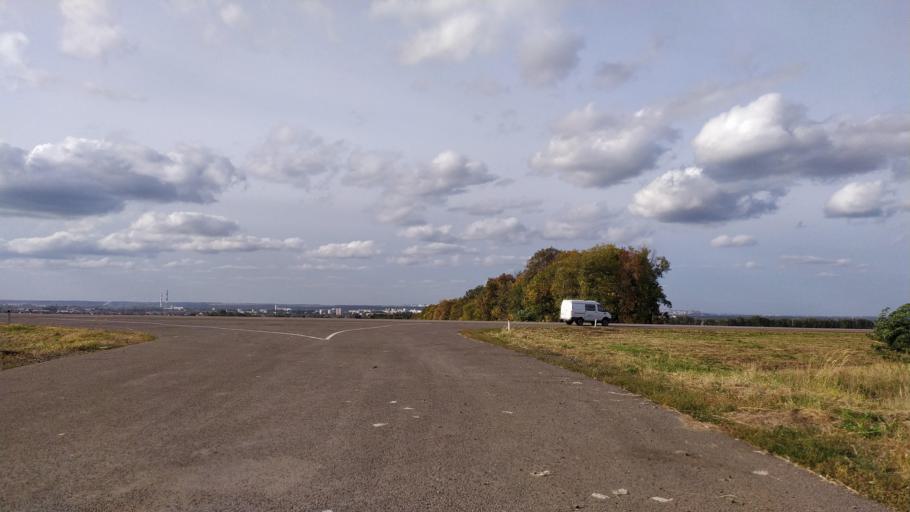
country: RU
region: Kursk
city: Kursk
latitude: 51.6140
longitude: 36.1645
